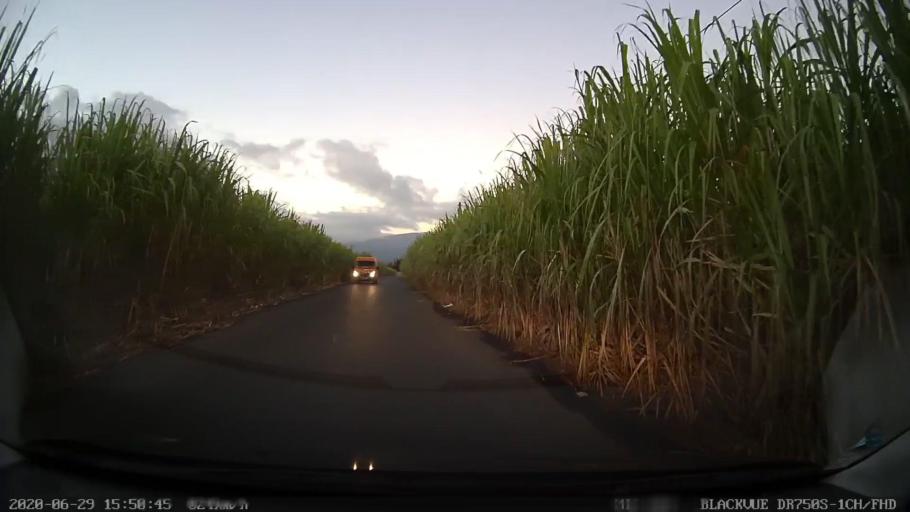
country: RE
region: Reunion
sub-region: Reunion
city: Bras-Panon
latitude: -20.9908
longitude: 55.6929
